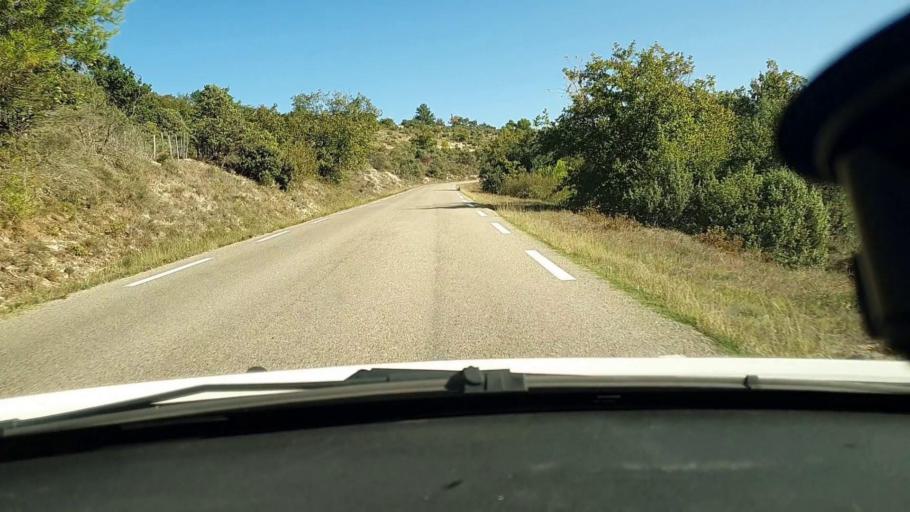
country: FR
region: Languedoc-Roussillon
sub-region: Departement du Gard
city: Goudargues
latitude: 44.2817
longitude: 4.4567
